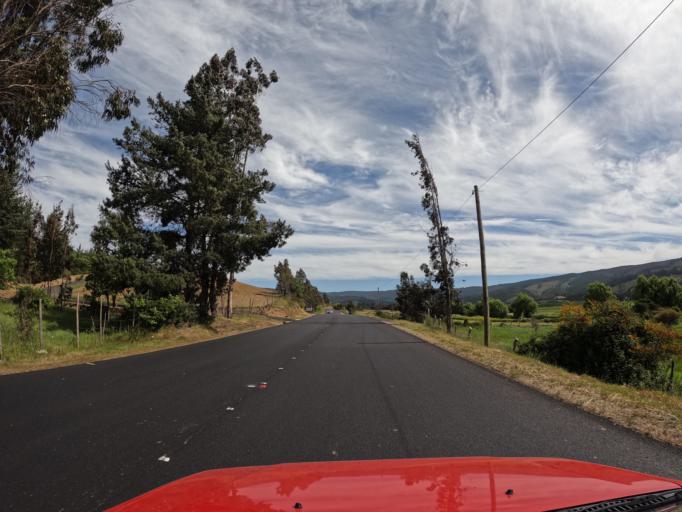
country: CL
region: Maule
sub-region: Provincia de Talca
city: Constitucion
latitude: -35.0691
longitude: -72.0380
